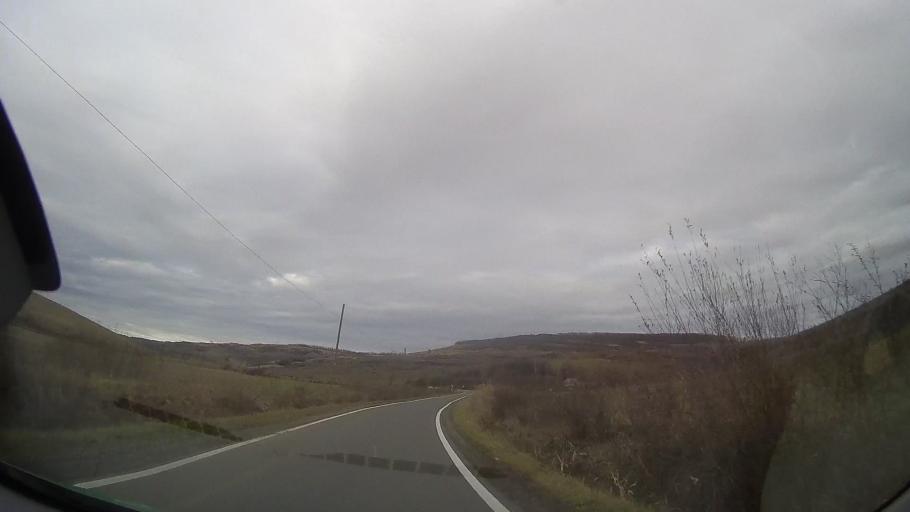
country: RO
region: Mures
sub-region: Comuna Cozma
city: Cozma
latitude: 46.7927
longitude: 24.5426
